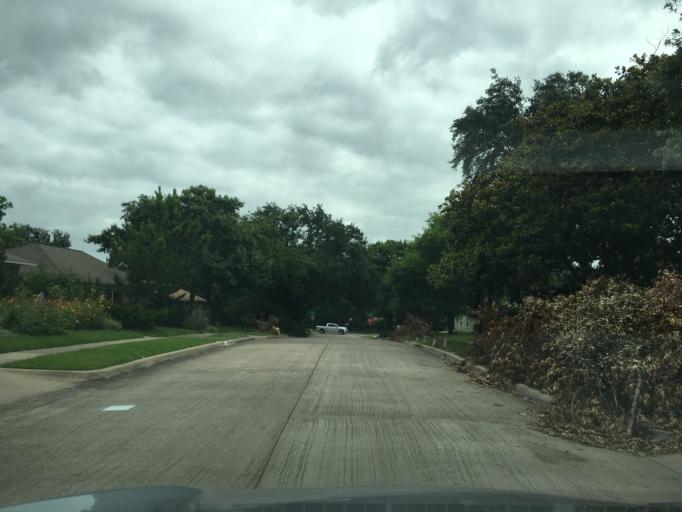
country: US
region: Texas
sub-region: Dallas County
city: Highland Park
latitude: 32.8607
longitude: -96.7426
